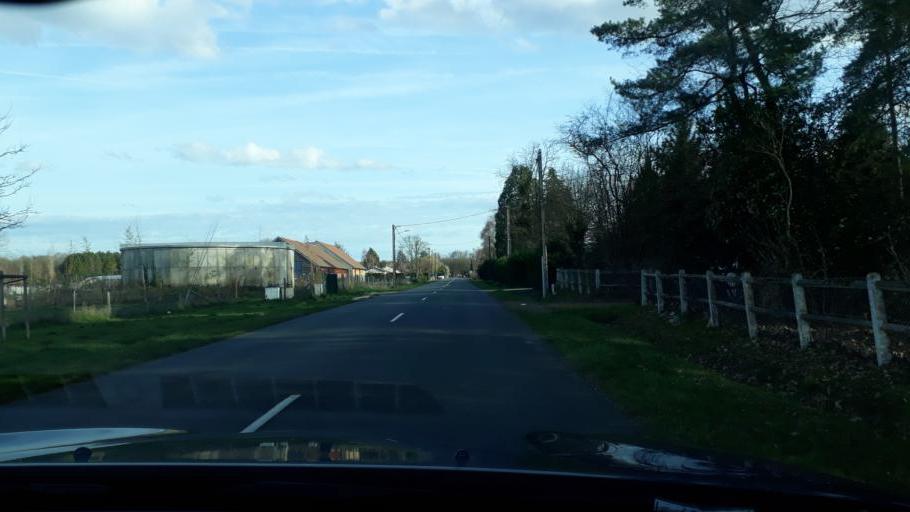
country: FR
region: Centre
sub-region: Departement du Loiret
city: Chilleurs-aux-Bois
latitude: 48.0576
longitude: 2.1734
